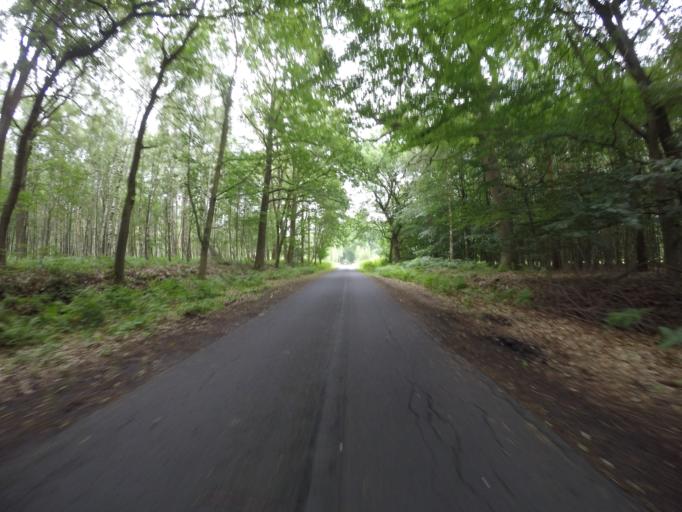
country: DE
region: North Rhine-Westphalia
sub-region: Regierungsbezirk Dusseldorf
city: Hunxe
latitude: 51.6241
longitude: 6.8150
